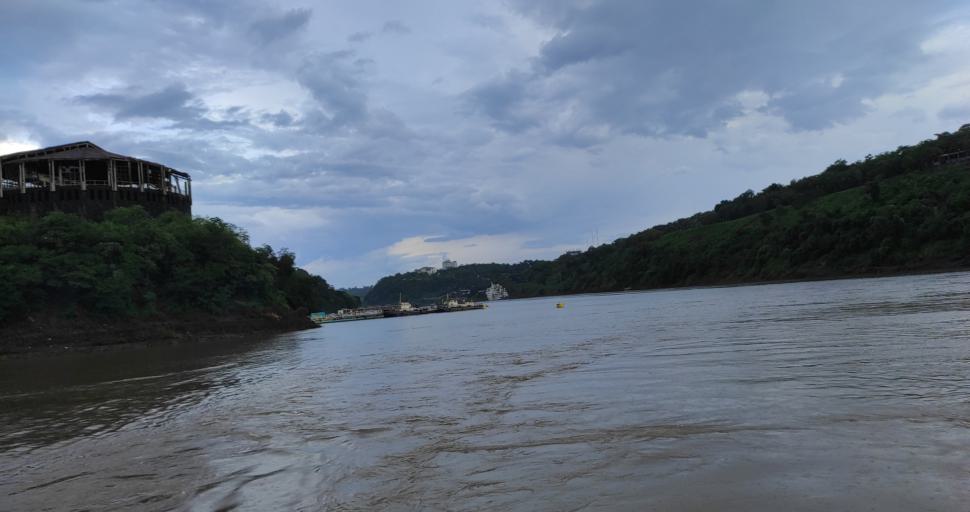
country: AR
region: Misiones
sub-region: Departamento de Iguazu
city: Puerto Iguazu
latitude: -25.5916
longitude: -54.5922
